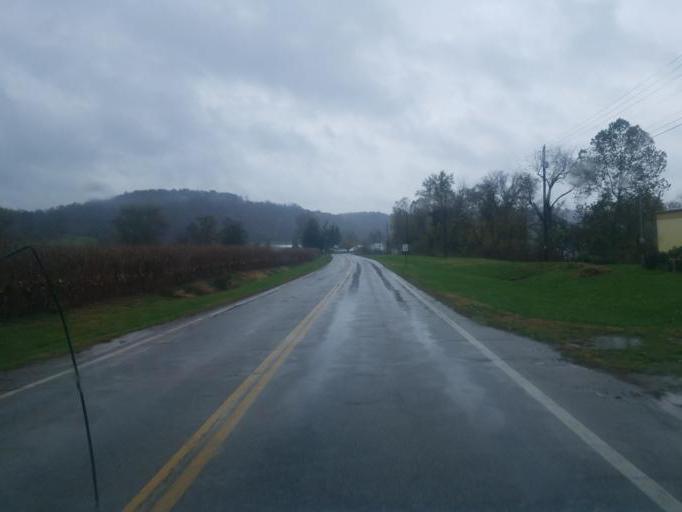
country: US
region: Ohio
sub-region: Morgan County
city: McConnelsville
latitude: 39.6425
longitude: -81.8447
